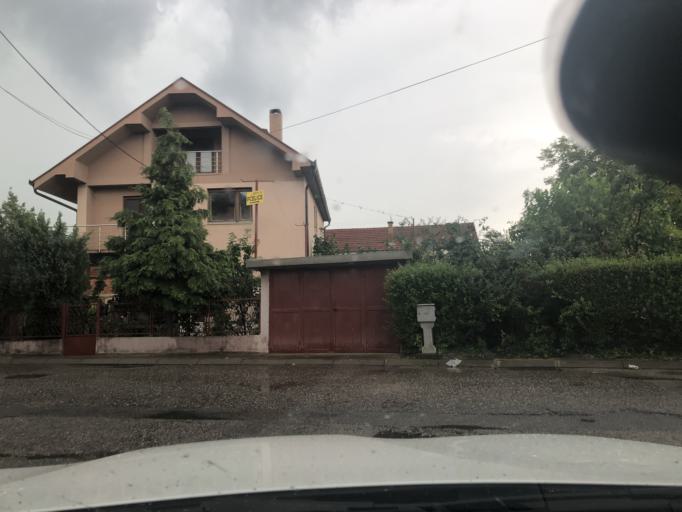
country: RS
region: Central Serbia
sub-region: Jablanicki Okrug
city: Leskovac
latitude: 42.9999
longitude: 21.9507
